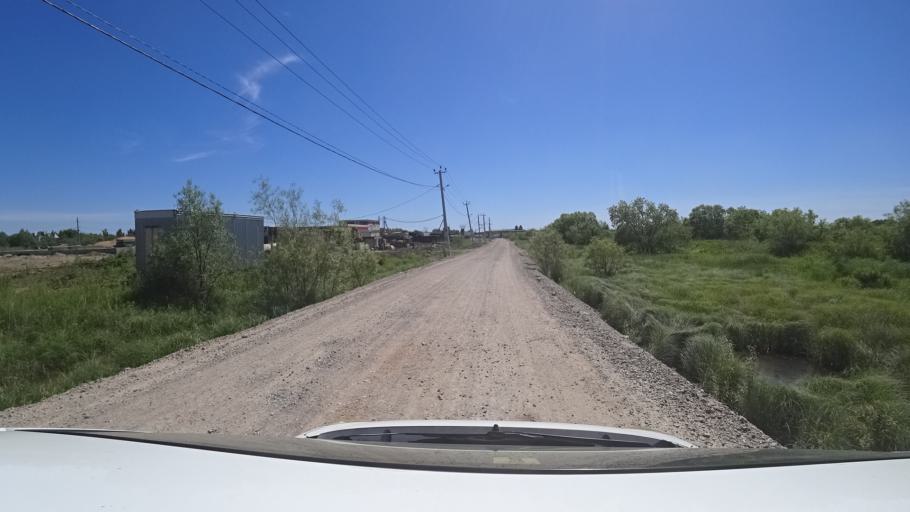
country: RU
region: Khabarovsk Krai
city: Topolevo
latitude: 48.4782
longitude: 135.1728
